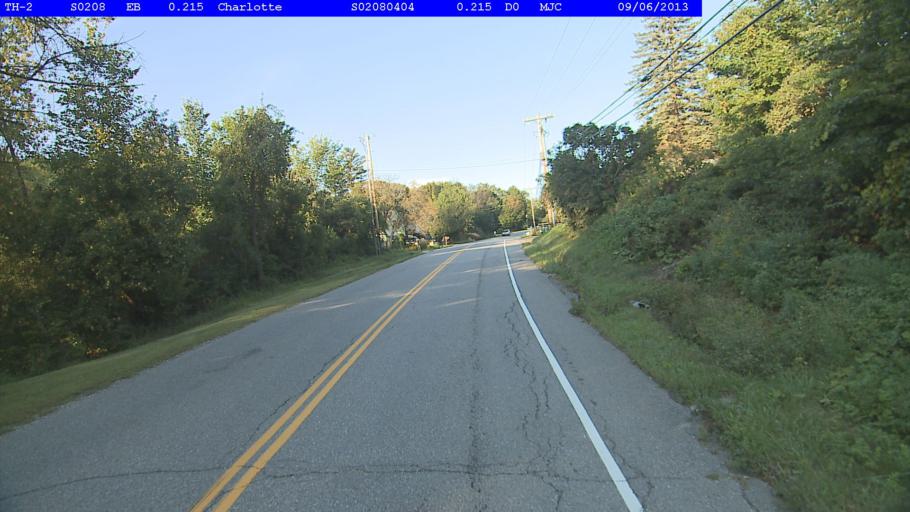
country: US
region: Vermont
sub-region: Chittenden County
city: Hinesburg
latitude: 44.3129
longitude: -73.2434
